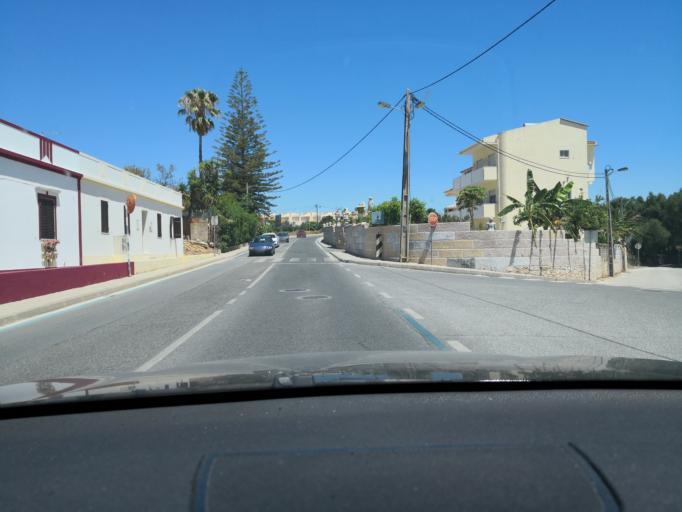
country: PT
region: Faro
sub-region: Albufeira
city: Albufeira
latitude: 37.0999
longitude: -8.2169
